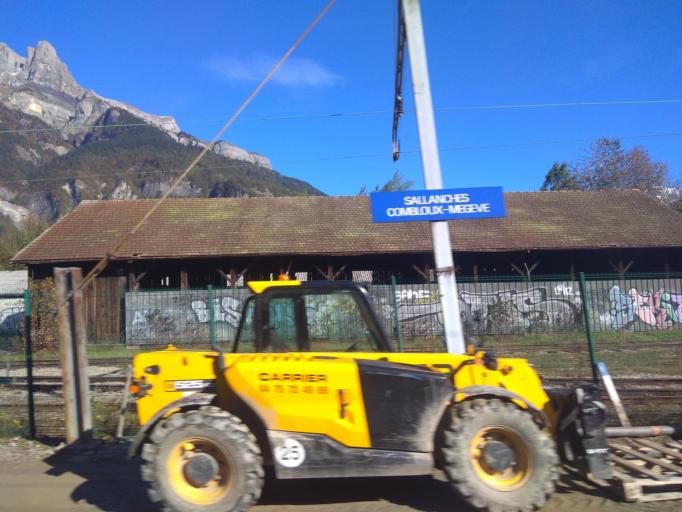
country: FR
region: Rhone-Alpes
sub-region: Departement de la Haute-Savoie
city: Sallanches
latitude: 45.9342
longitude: 6.6368
